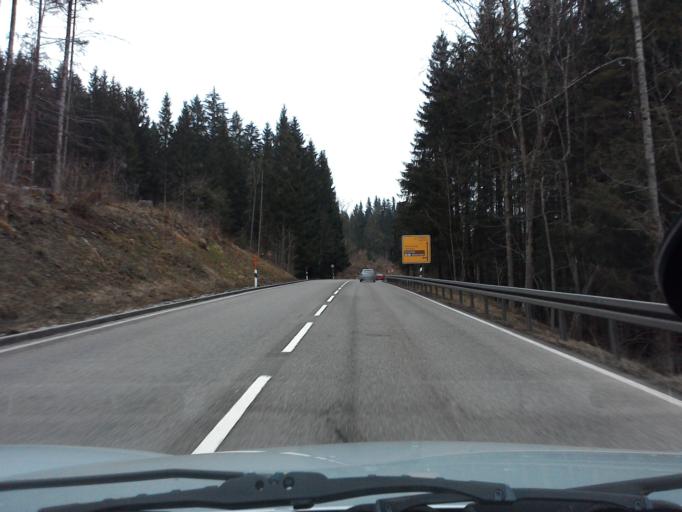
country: DE
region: Bavaria
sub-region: Swabia
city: Bolsterlang
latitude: 47.4804
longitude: 10.2663
